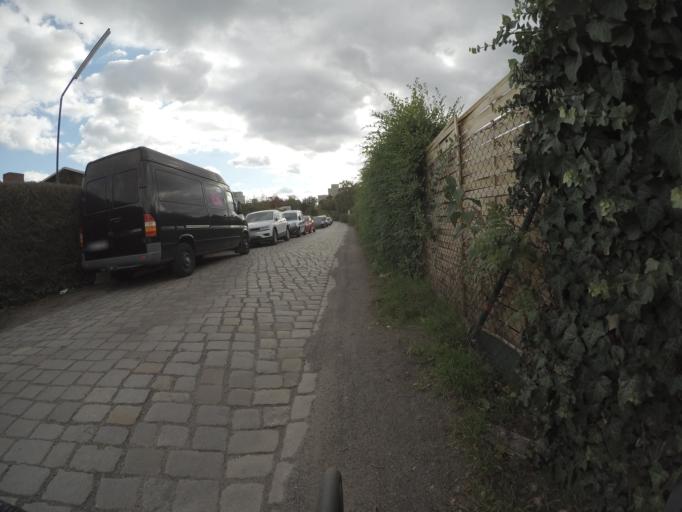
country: DE
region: Berlin
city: Charlottenburg-Nord
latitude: 52.5425
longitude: 13.3006
